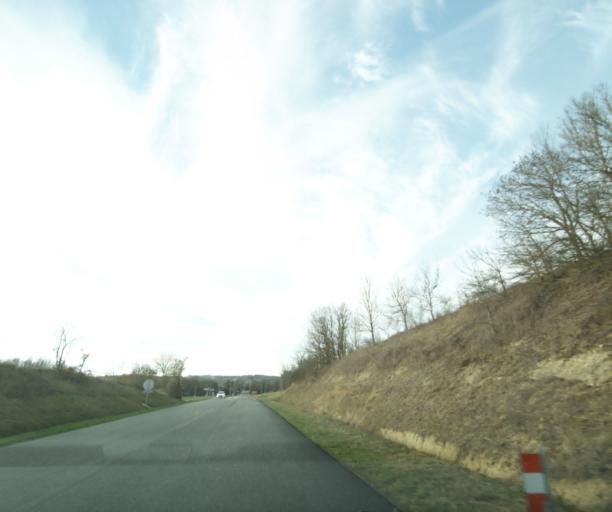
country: FR
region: Midi-Pyrenees
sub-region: Departement du Gers
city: Jegun
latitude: 43.6928
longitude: 0.4669
